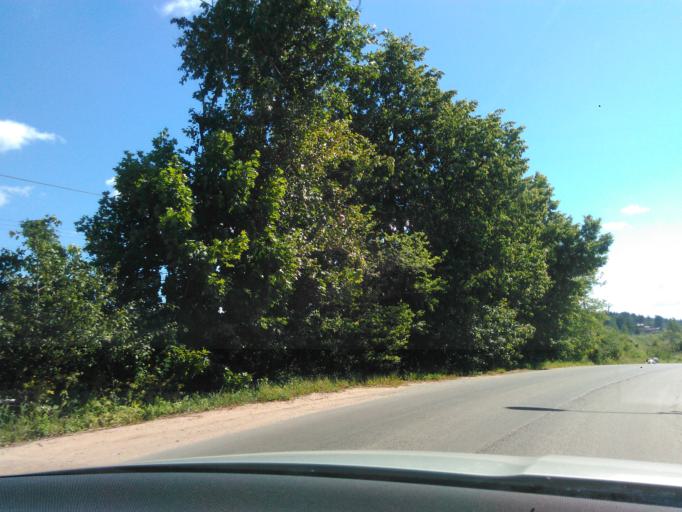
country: RU
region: Moskovskaya
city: Klin
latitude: 56.2365
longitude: 36.8317
